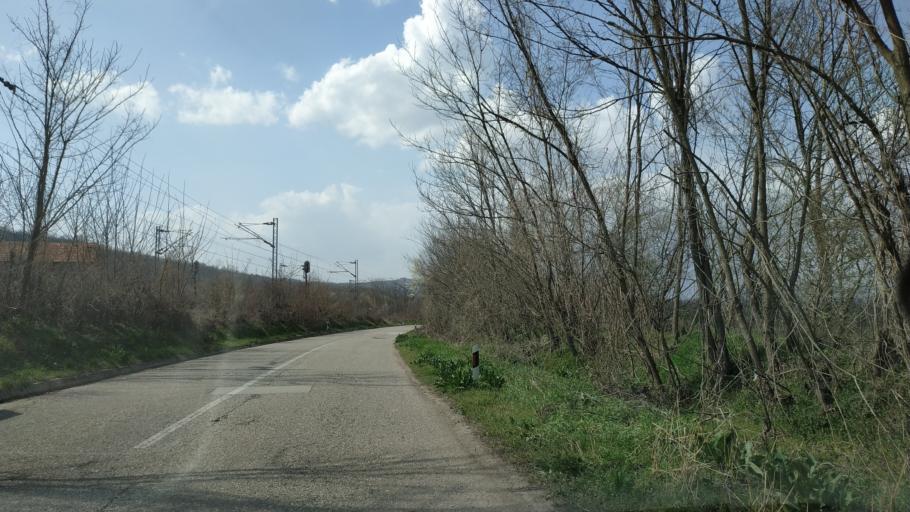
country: RS
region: Central Serbia
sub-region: Nisavski Okrug
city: Razanj
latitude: 43.5739
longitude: 21.5796
